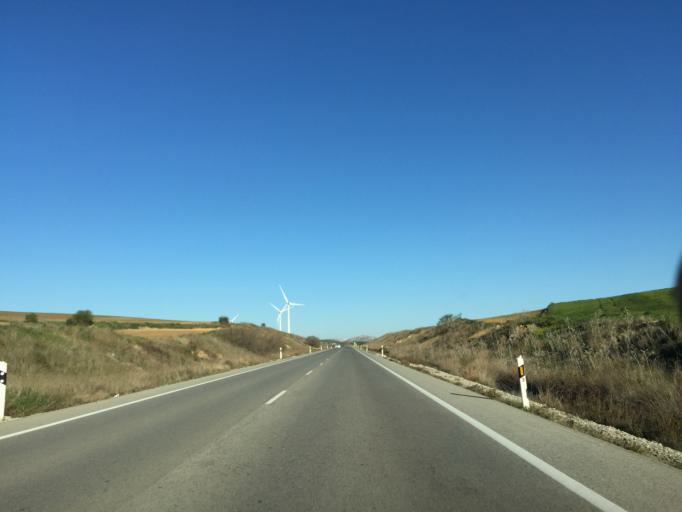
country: ES
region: Andalusia
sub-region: Provincia de Malaga
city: Ardales
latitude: 36.9260
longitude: -4.8498
